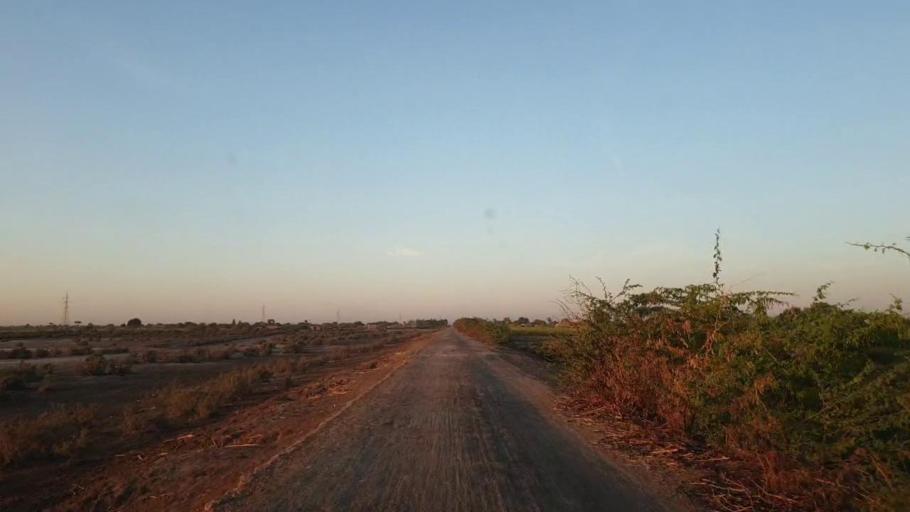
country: PK
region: Sindh
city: Kunri
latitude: 25.1396
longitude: 69.4443
